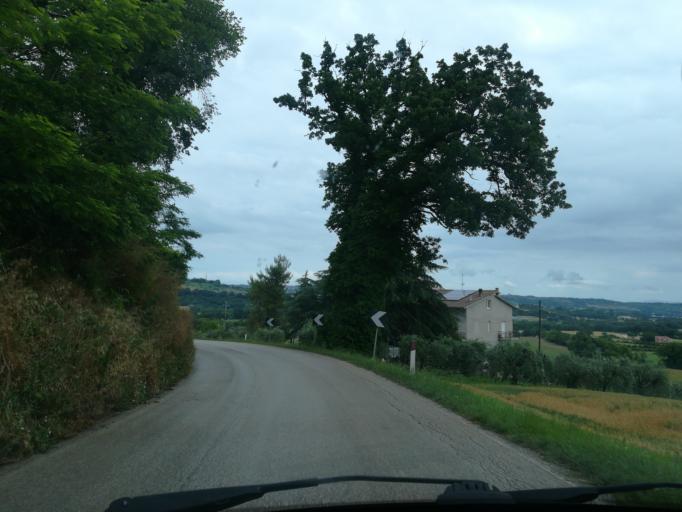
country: IT
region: The Marches
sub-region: Provincia di Macerata
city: Petriolo
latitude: 43.2270
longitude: 13.4641
